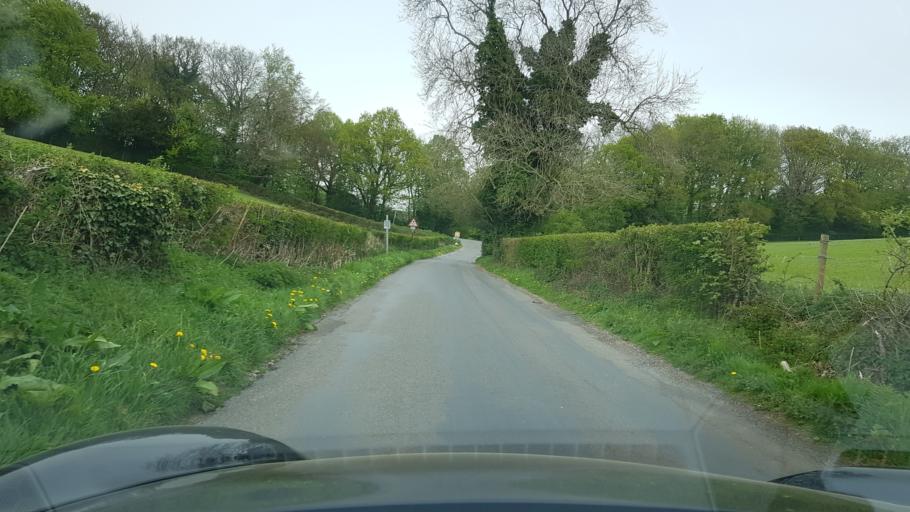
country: GB
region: England
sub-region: Surrey
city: East Horsley
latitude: 51.2374
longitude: -0.4048
